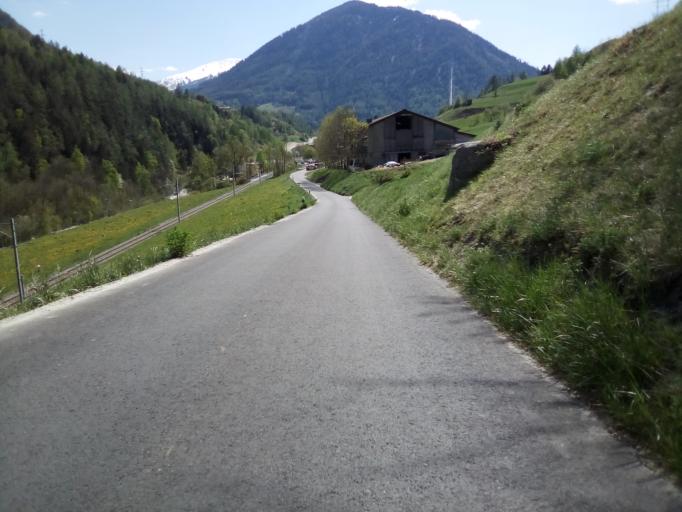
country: CH
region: Valais
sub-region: Entremont District
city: Orsieres
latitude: 46.0405
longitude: 7.1457
